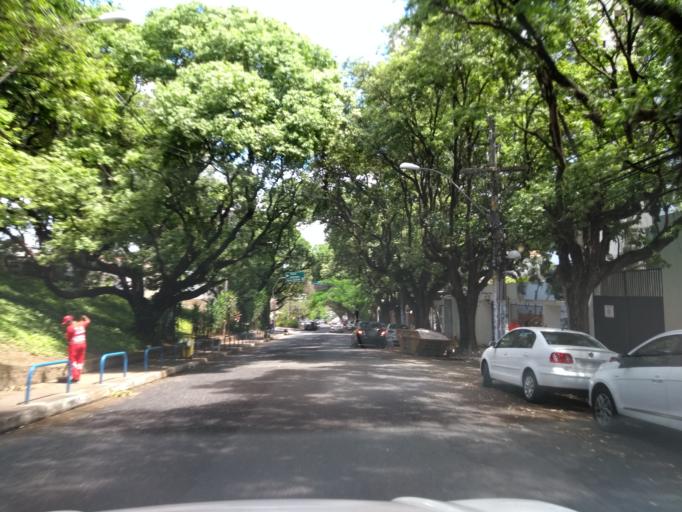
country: BR
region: Bahia
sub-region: Salvador
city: Salvador
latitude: -13.0003
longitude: -38.5241
